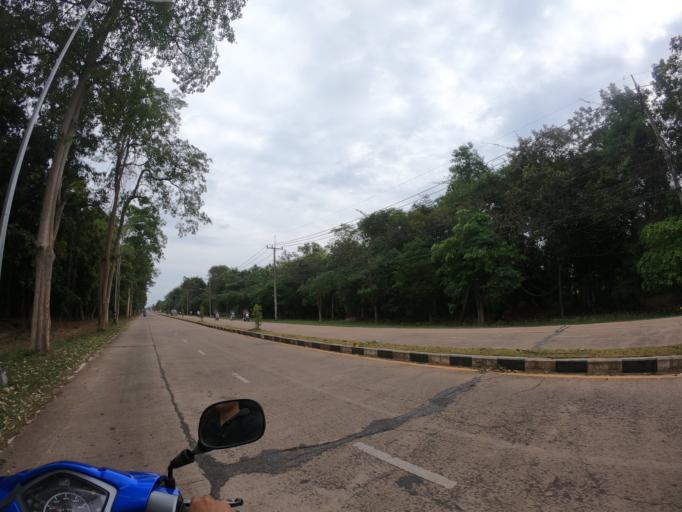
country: TH
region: Roi Et
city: Chiang Khwan
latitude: 16.1460
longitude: 103.8709
